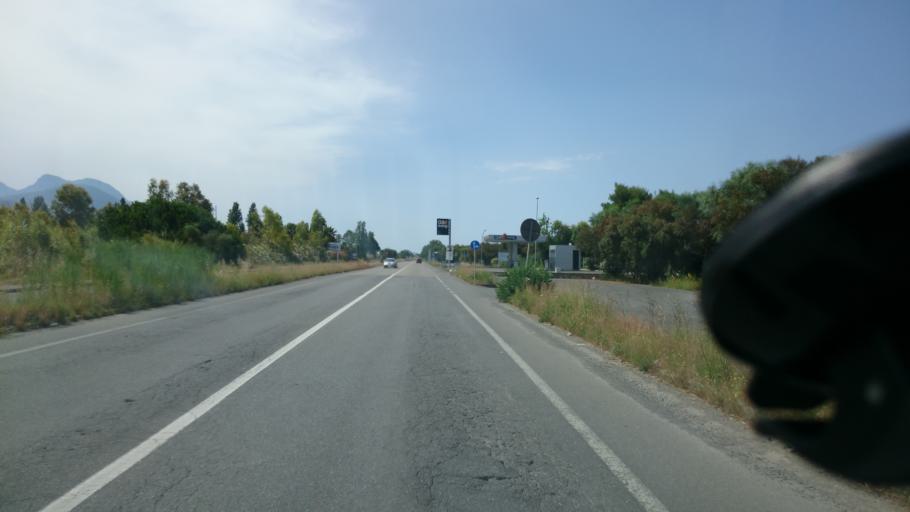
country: IT
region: Calabria
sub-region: Provincia di Cosenza
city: Scalea
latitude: 39.7950
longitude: 15.7930
